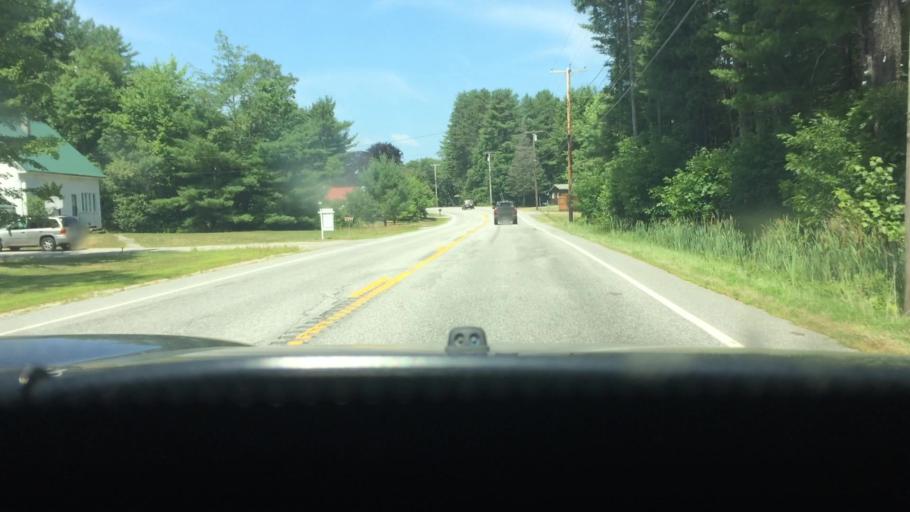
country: US
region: Maine
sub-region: Androscoggin County
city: Minot
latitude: 44.0924
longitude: -70.3472
